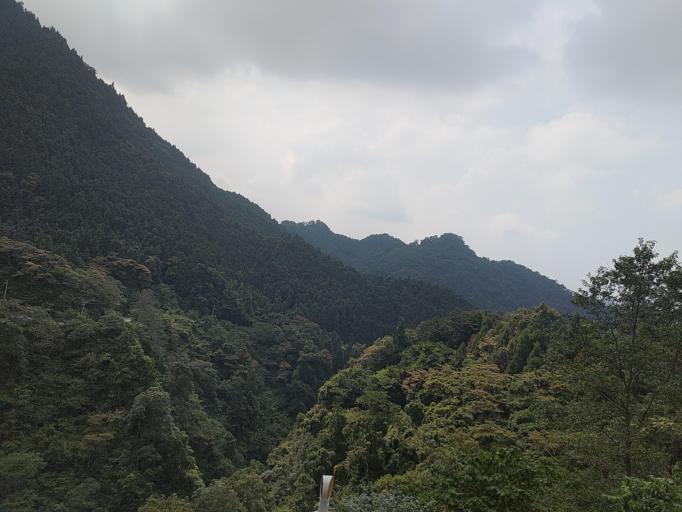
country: TW
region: Taiwan
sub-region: Hsinchu
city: Hsinchu
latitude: 24.6273
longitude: 121.0824
